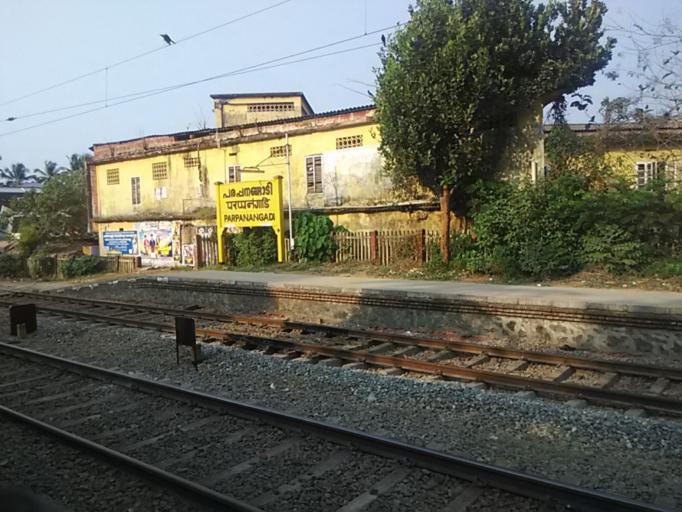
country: IN
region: Kerala
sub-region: Malappuram
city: Pariyapuram
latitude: 11.0483
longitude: 75.8598
